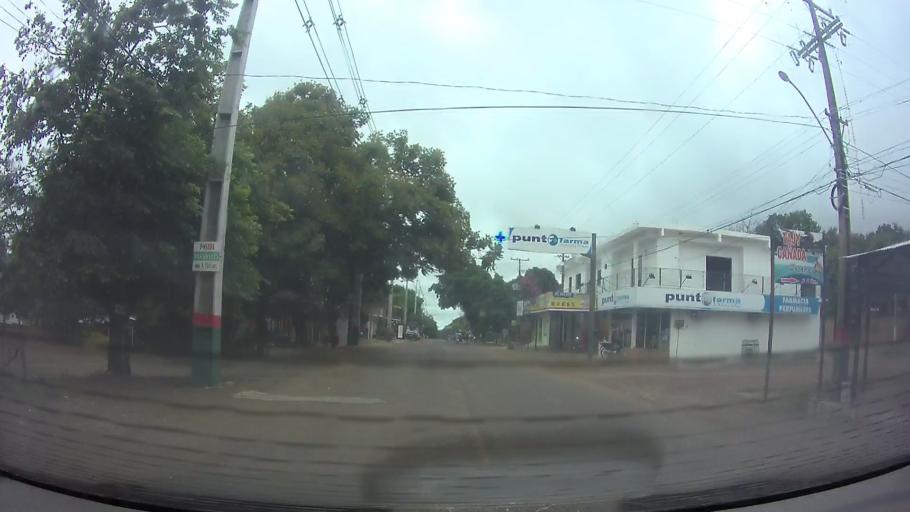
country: PY
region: Cordillera
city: Altos
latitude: -25.2660
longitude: -57.2504
